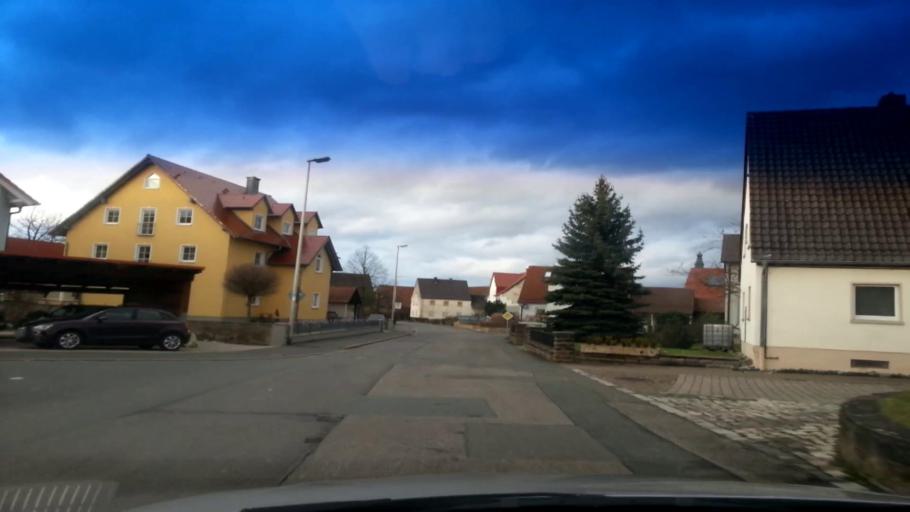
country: DE
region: Bavaria
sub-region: Upper Franconia
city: Zapfendorf
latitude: 50.0152
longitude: 10.9320
